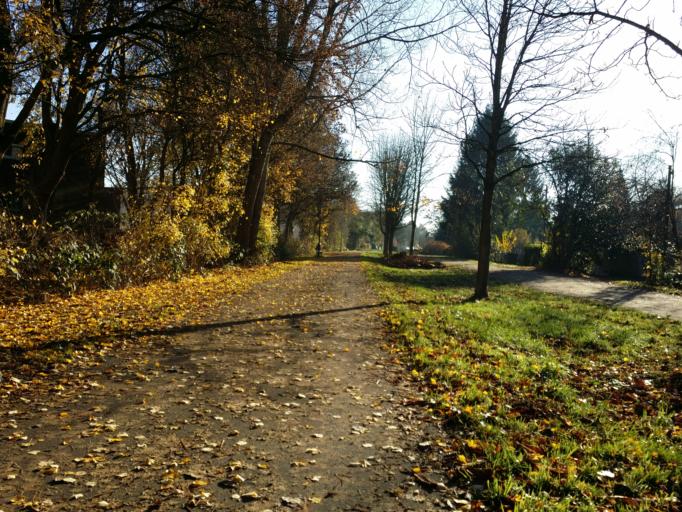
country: DE
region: Bremen
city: Bremen
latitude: 53.0716
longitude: 8.8749
